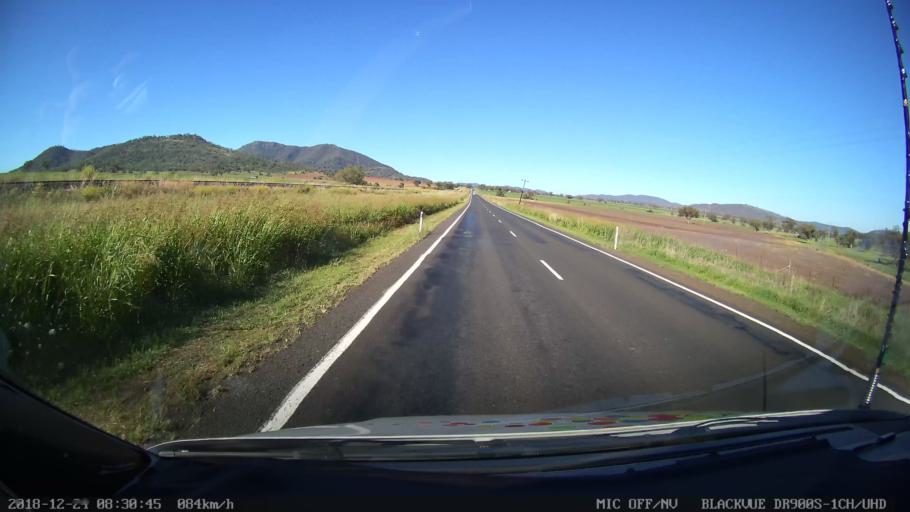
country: AU
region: New South Wales
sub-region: Tamworth Municipality
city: Phillip
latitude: -31.2693
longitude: 150.7206
